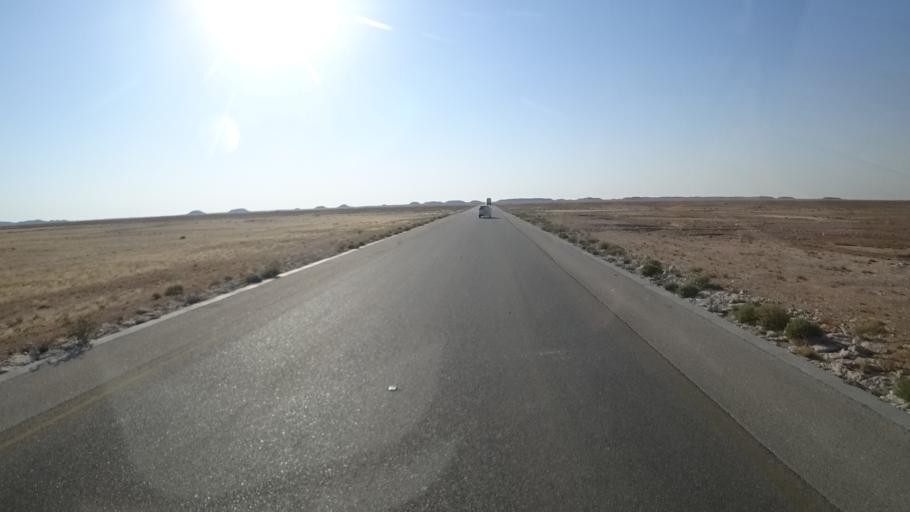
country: OM
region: Zufar
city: Salalah
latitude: 17.6424
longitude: 53.8377
